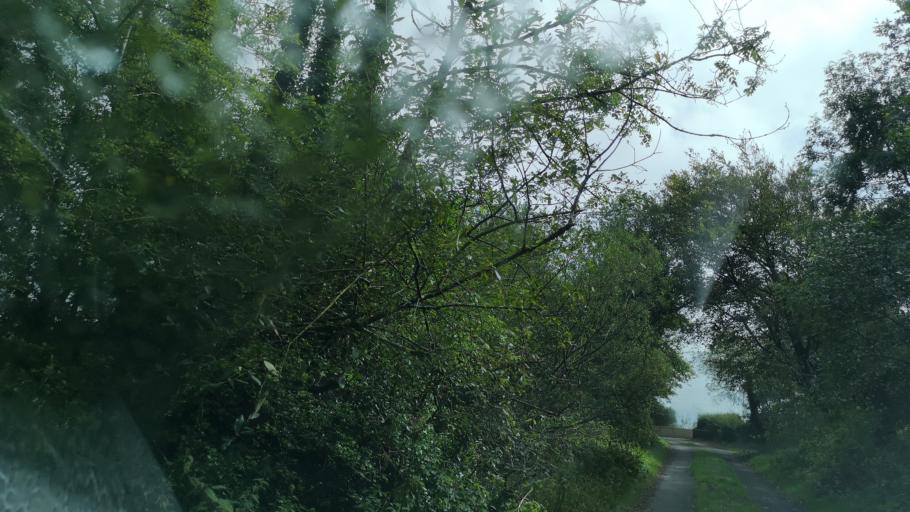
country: IE
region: Connaught
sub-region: County Galway
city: Athenry
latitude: 53.3025
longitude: -8.6286
